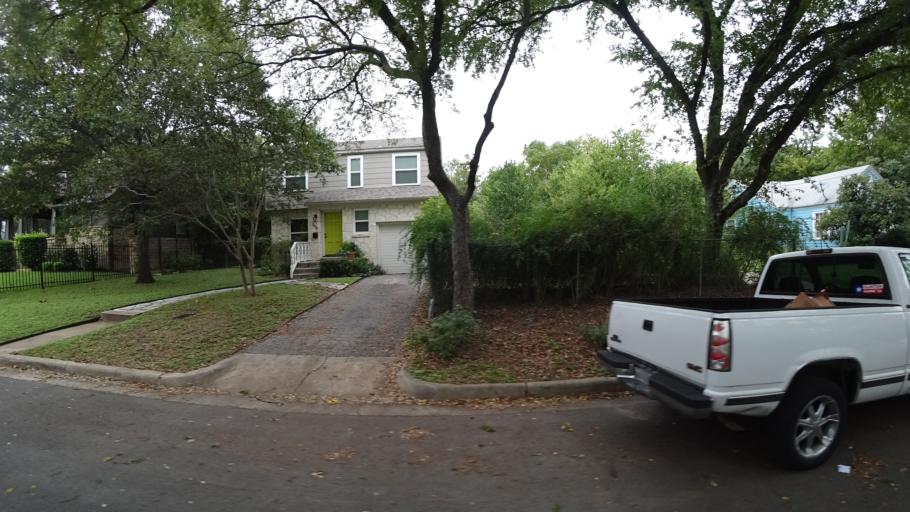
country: US
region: Texas
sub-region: Travis County
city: Austin
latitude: 30.2966
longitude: -97.7208
